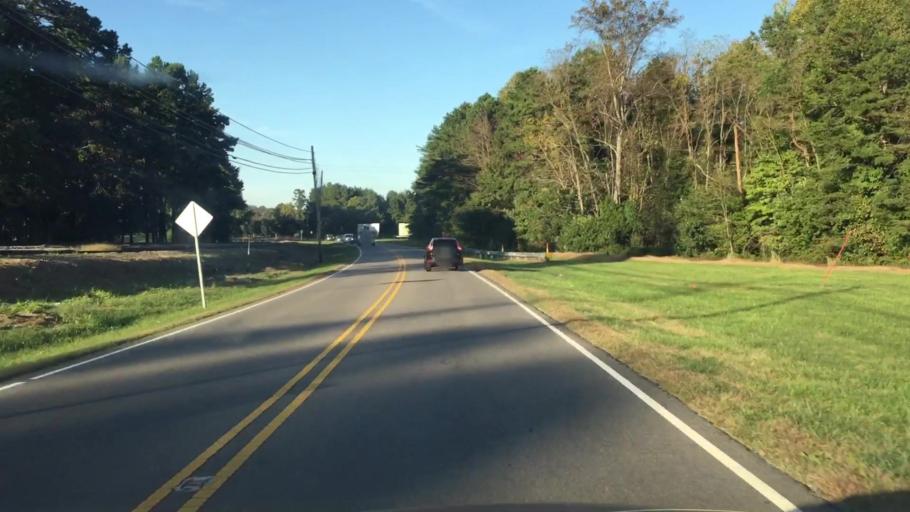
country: US
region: North Carolina
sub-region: Iredell County
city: Mooresville
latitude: 35.5655
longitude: -80.8292
